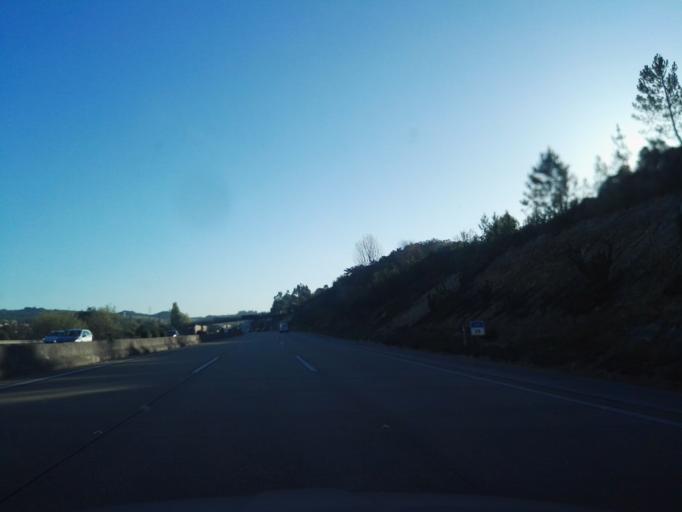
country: PT
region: Lisbon
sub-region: Loures
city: Bucelas
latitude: 38.8991
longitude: -9.1092
